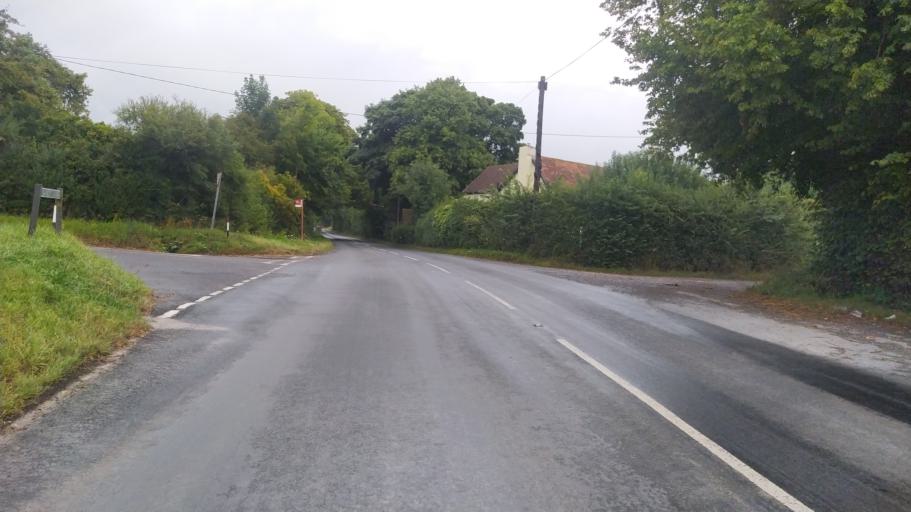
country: GB
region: England
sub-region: Wiltshire
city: Ansty
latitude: 51.0152
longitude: -2.0966
